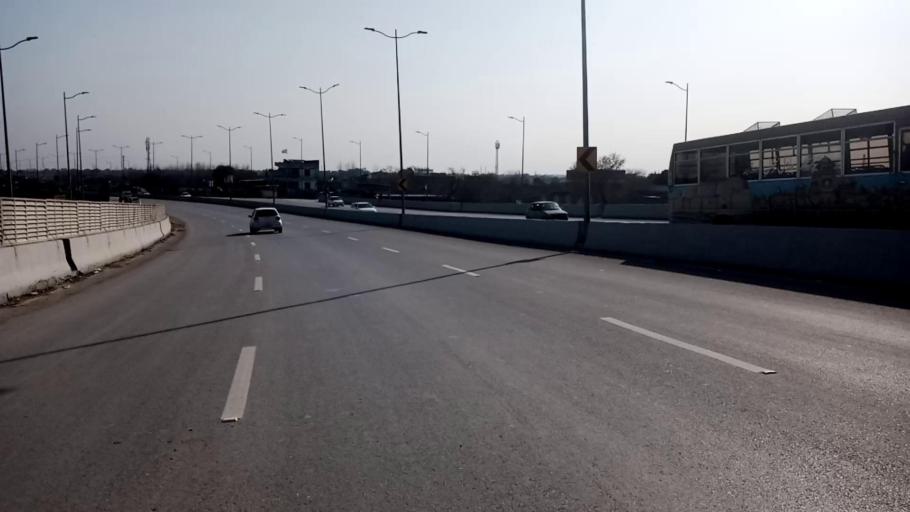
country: PK
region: Khyber Pakhtunkhwa
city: Peshawar
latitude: 34.0352
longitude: 71.5412
